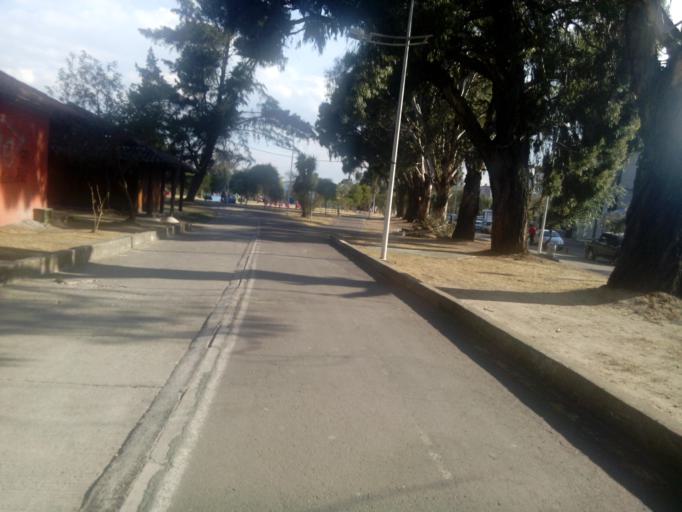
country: EC
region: Pichincha
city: Quito
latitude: -0.1779
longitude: -78.4840
